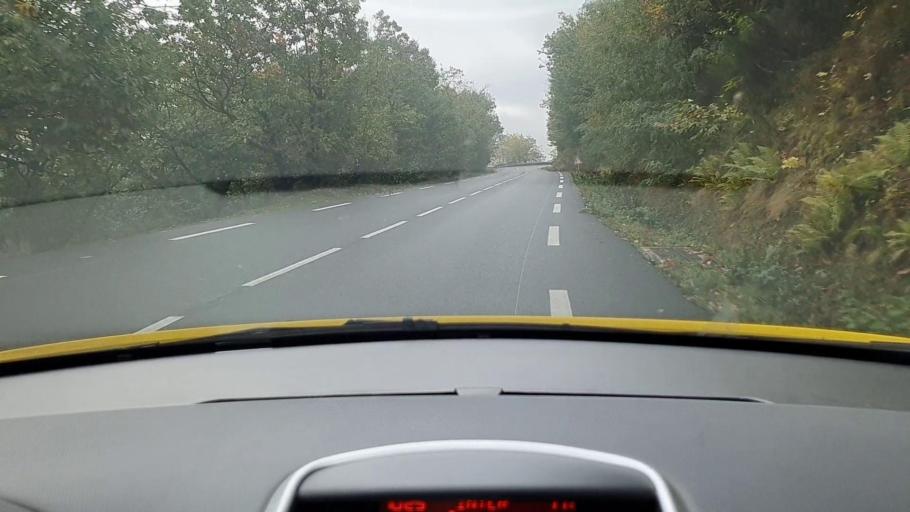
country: FR
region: Languedoc-Roussillon
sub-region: Departement du Gard
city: Valleraugue
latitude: 44.0874
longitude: 3.5878
